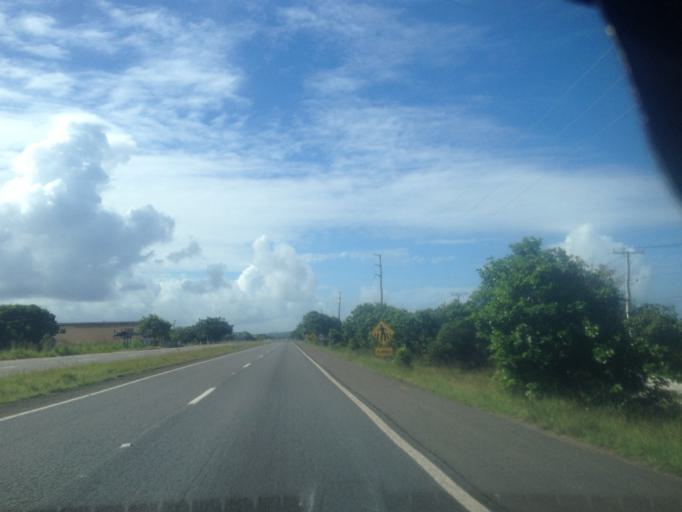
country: BR
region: Bahia
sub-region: Mata De Sao Joao
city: Mata de Sao Joao
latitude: -12.6343
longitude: -38.0675
